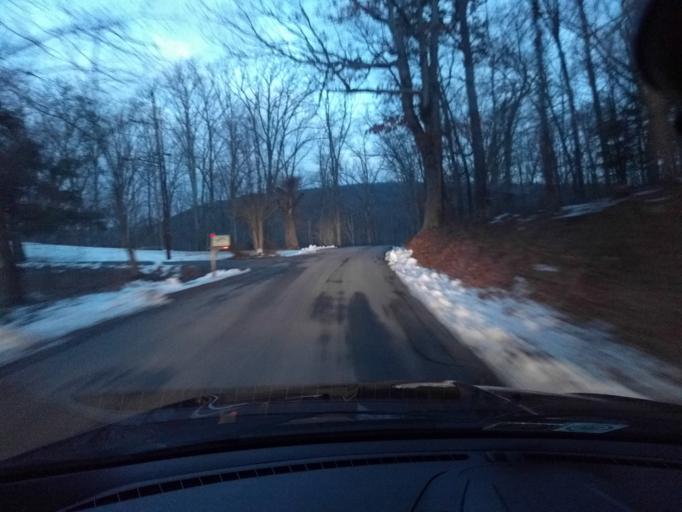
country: US
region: Virginia
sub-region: Alleghany County
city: Clifton Forge
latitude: 37.8488
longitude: -79.8465
